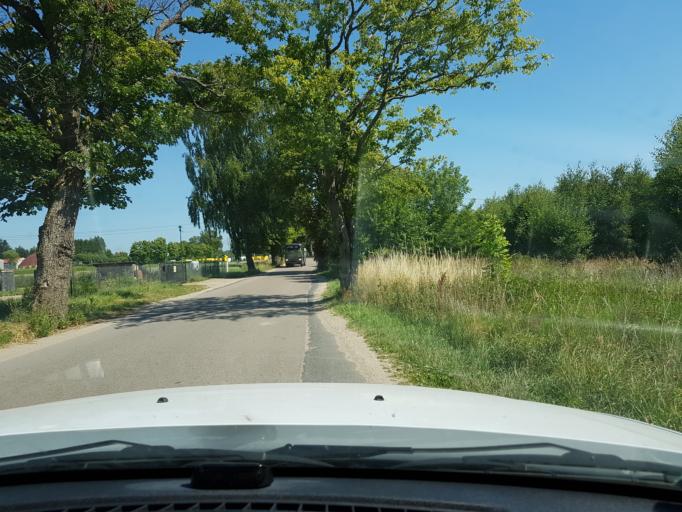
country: PL
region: West Pomeranian Voivodeship
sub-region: Koszalin
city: Koszalin
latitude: 54.1686
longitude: 16.0924
